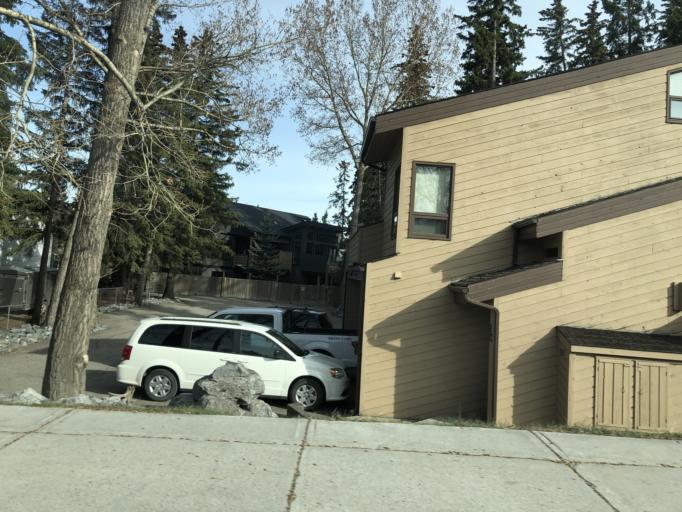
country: CA
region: Alberta
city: Canmore
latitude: 51.0864
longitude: -115.3644
